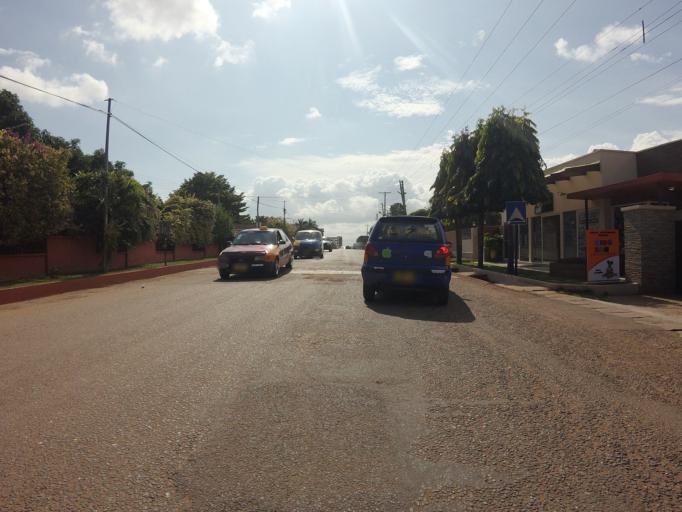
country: GH
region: Greater Accra
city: Medina Estates
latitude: 5.6688
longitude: -0.1841
